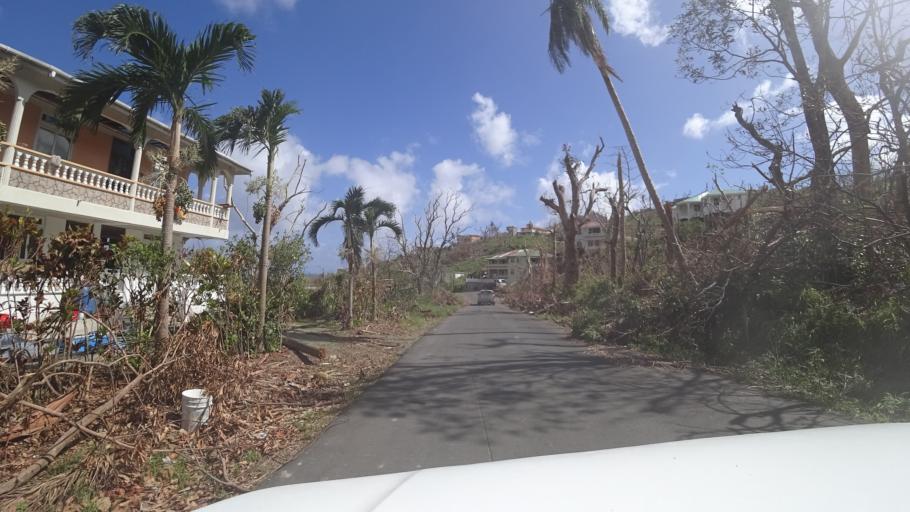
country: DM
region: Saint Patrick
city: Berekua
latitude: 15.2486
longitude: -61.3173
